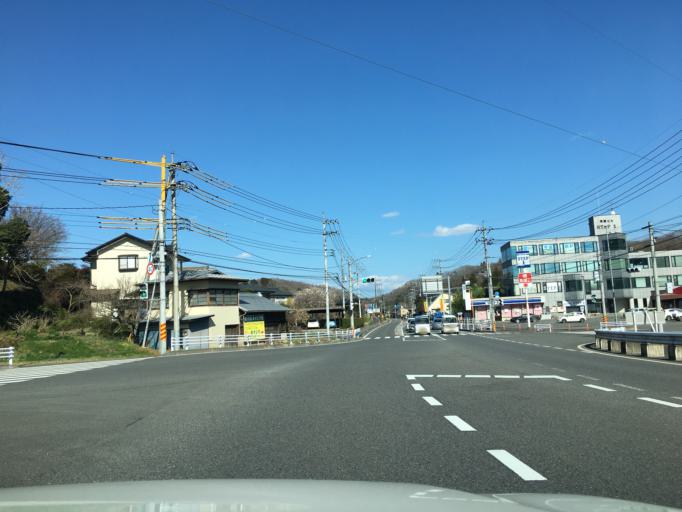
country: JP
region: Tochigi
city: Motegi
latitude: 36.5318
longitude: 140.2019
